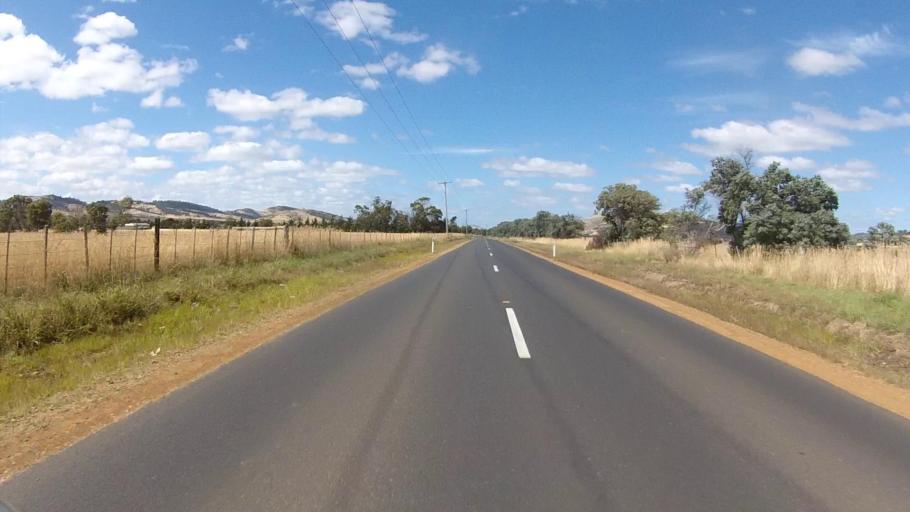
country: AU
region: Tasmania
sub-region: Clarence
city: Cambridge
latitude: -42.7133
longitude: 147.4306
